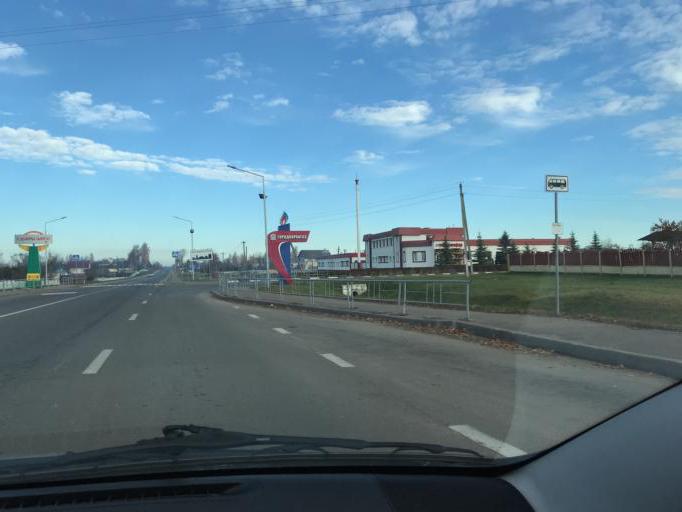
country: BY
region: Vitebsk
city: Haradok
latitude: 55.4727
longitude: 29.9697
